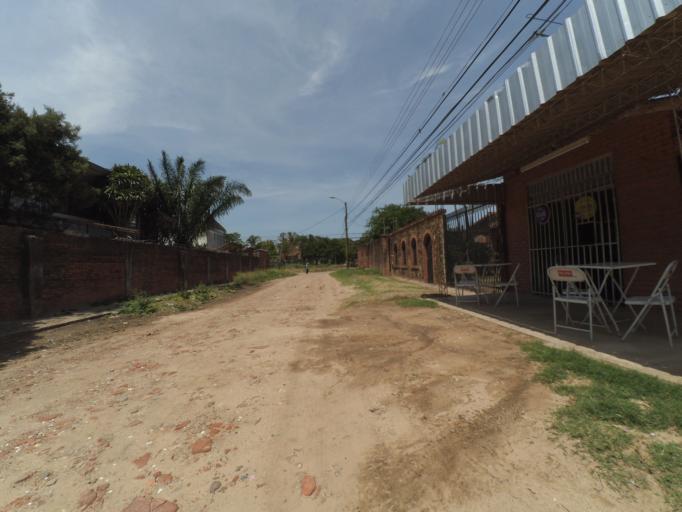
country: BO
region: Santa Cruz
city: Santa Cruz de la Sierra
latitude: -17.8236
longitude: -63.2242
